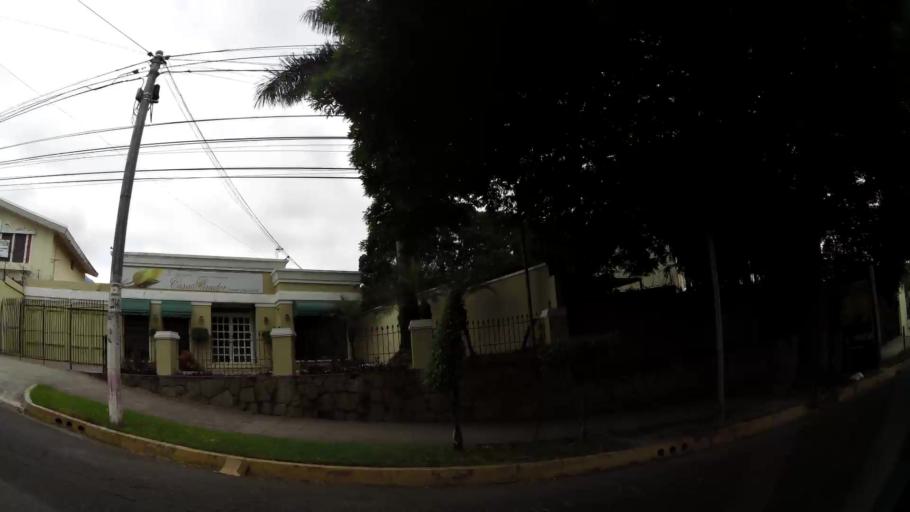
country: SV
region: San Salvador
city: Mejicanos
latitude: 13.7105
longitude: -89.2454
